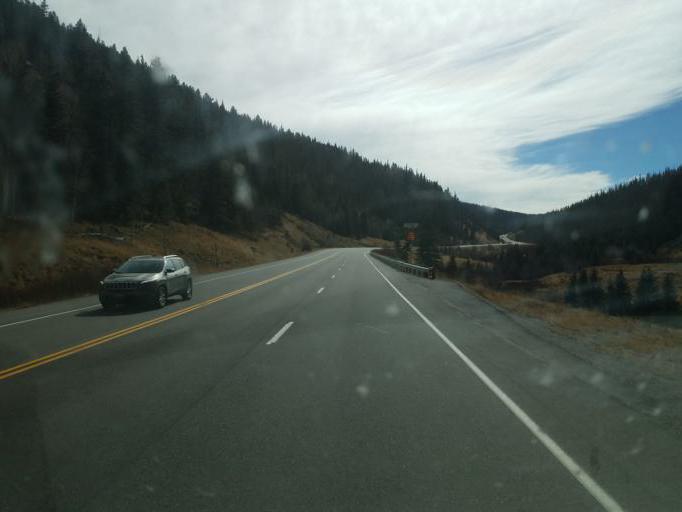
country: US
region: Colorado
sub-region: Mineral County
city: Creede
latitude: 37.5372
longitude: -106.7721
